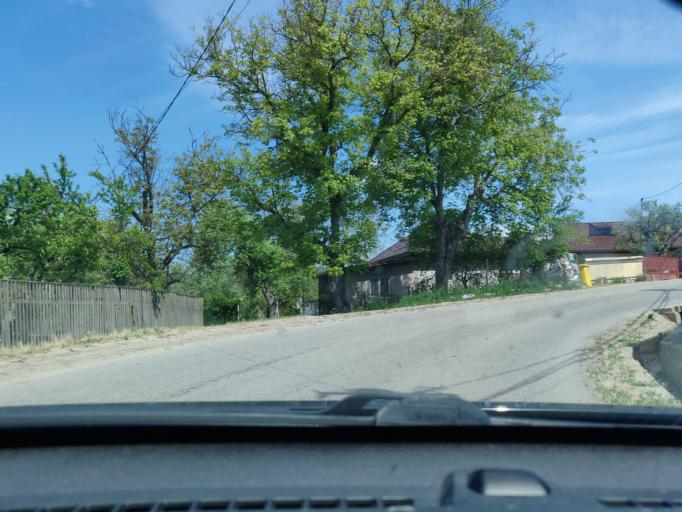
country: RO
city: Vizantea-Manastireasca
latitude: 45.9730
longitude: 26.8127
